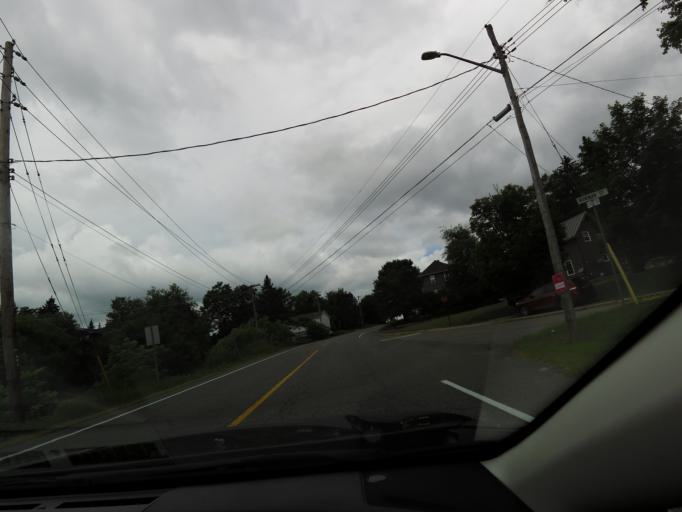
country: CA
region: Ontario
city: Bracebridge
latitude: 45.0365
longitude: -79.3052
